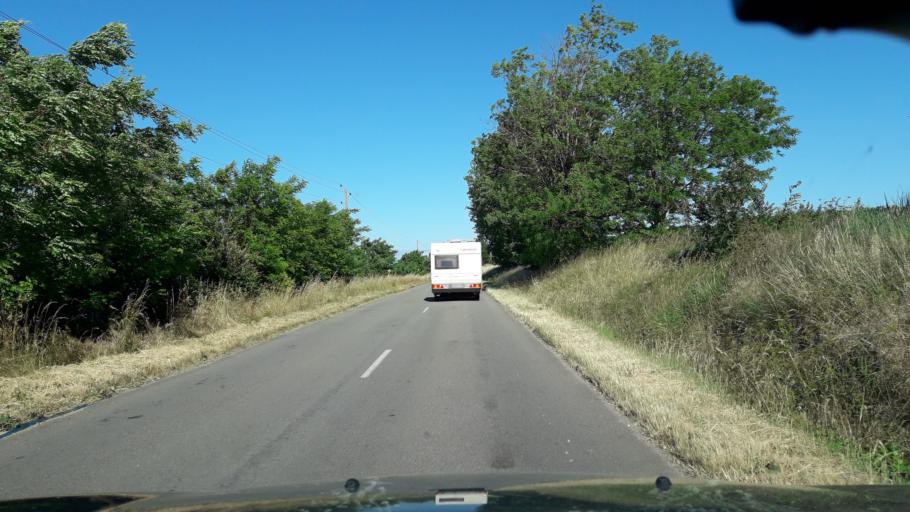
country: FR
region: Rhone-Alpes
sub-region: Departement de la Drome
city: Livron-sur-Drome
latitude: 44.7571
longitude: 4.8429
